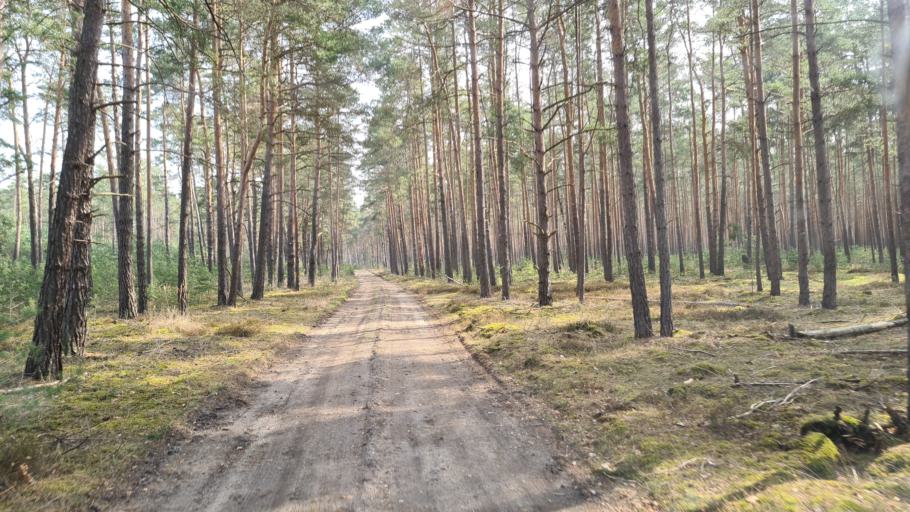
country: DE
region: Brandenburg
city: Trobitz
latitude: 51.6325
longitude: 13.4090
